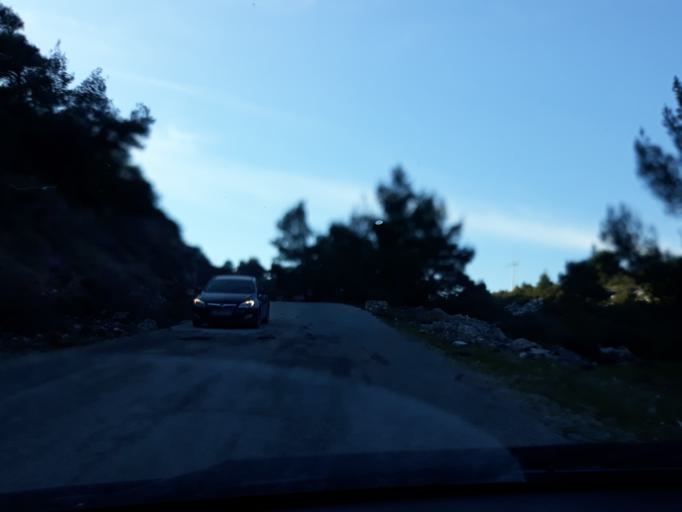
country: GR
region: Attica
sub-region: Nomarchia Dytikis Attikis
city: Fyli
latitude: 38.1570
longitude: 23.6300
